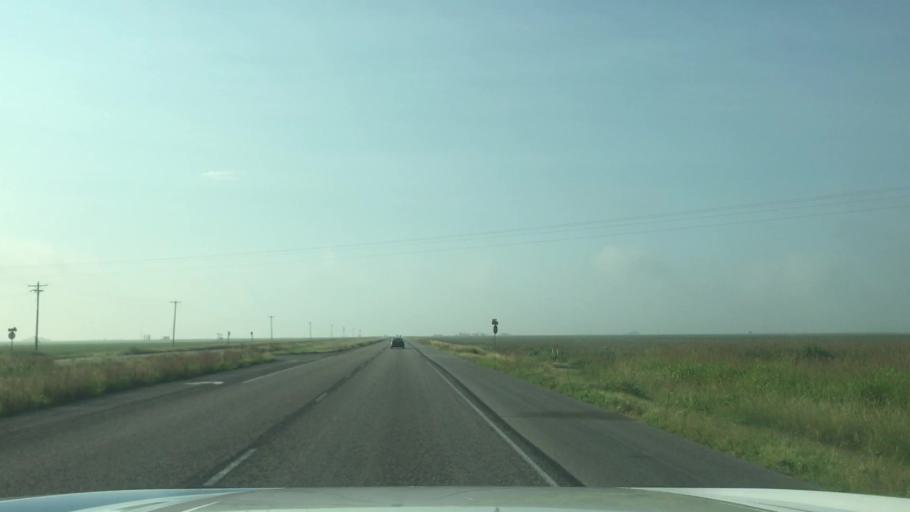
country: US
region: Texas
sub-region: Lubbock County
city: Slaton
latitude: 33.3313
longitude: -101.5344
